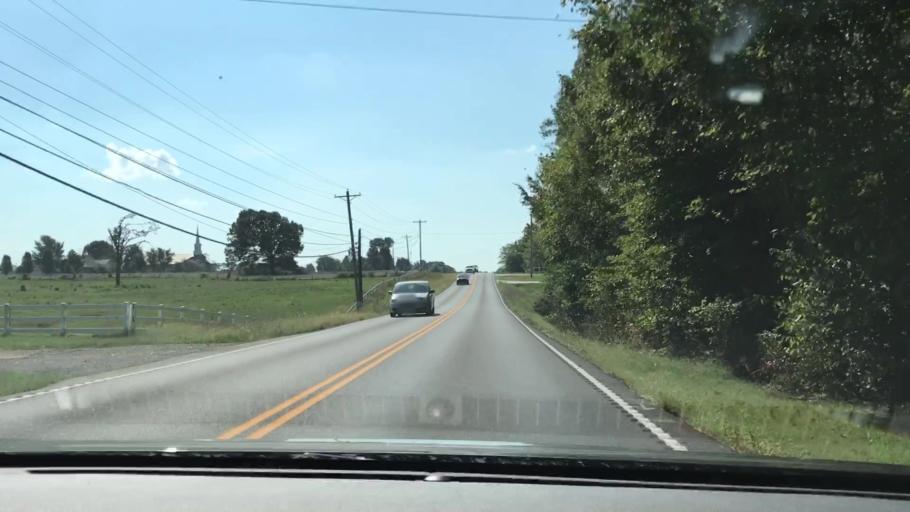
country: US
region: Kentucky
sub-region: Marshall County
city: Benton
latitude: 36.8203
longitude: -88.3504
